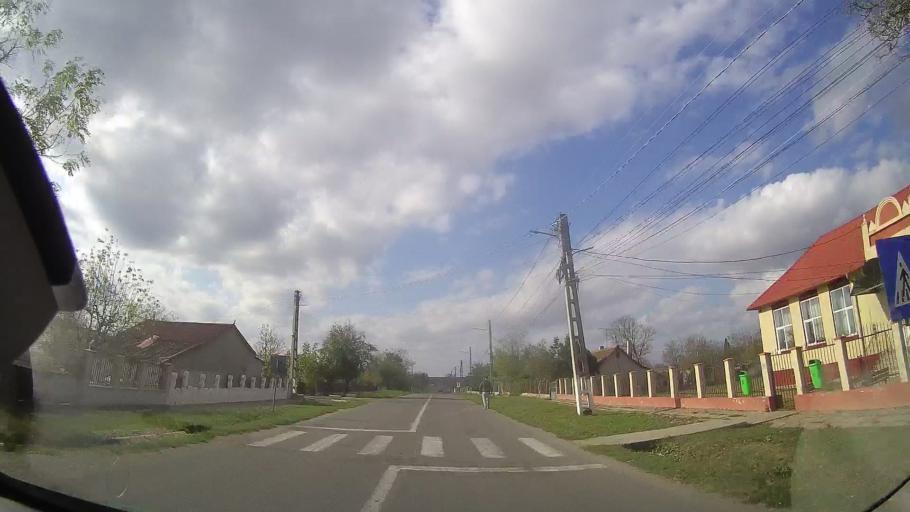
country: RO
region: Constanta
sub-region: Comuna Pecineaga
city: Pecineaga
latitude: 43.8951
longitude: 28.5037
